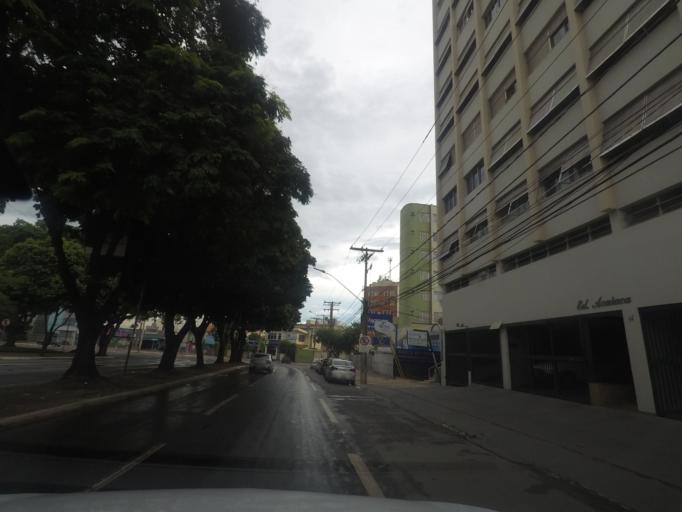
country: BR
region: Goias
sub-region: Goiania
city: Goiania
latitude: -16.6799
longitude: -49.2546
